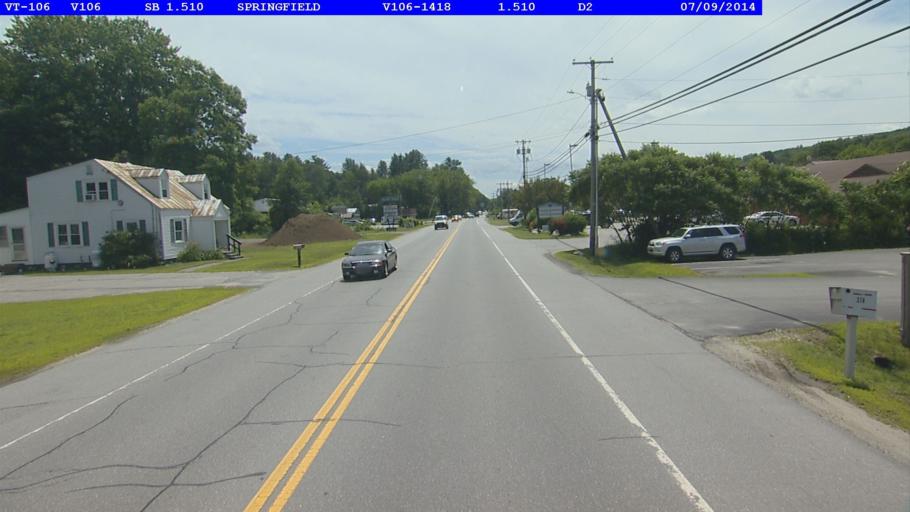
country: US
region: Vermont
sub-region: Windsor County
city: Springfield
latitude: 43.3222
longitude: -72.5075
